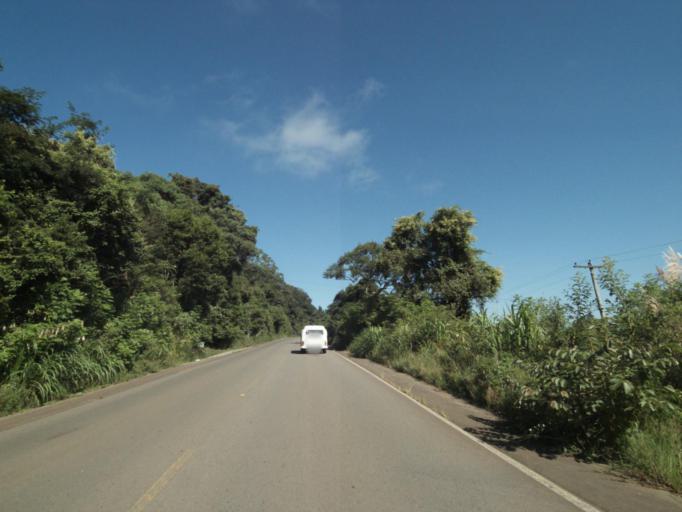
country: BR
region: Rio Grande do Sul
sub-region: Bento Goncalves
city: Bento Goncalves
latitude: -29.1204
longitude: -51.5571
